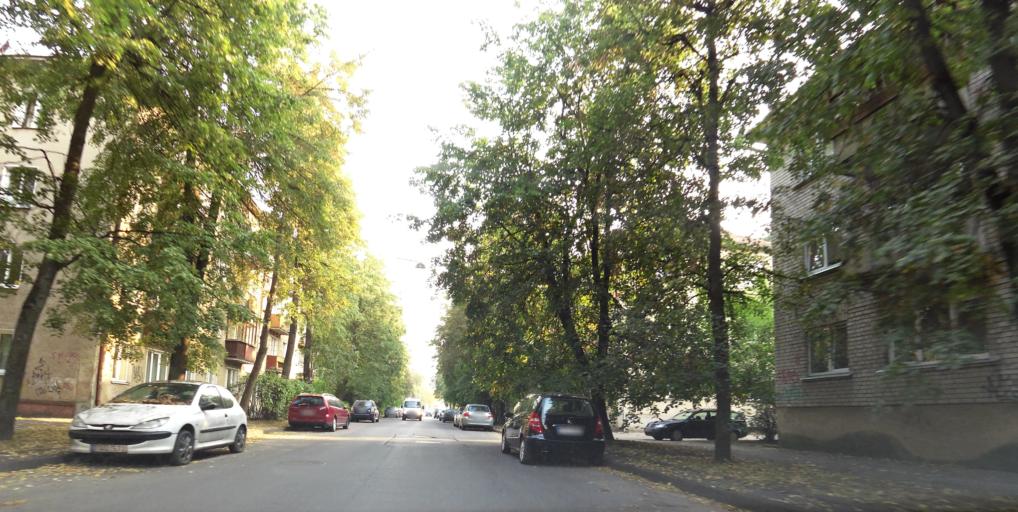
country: LT
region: Vilnius County
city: Rasos
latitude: 54.7073
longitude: 25.3145
